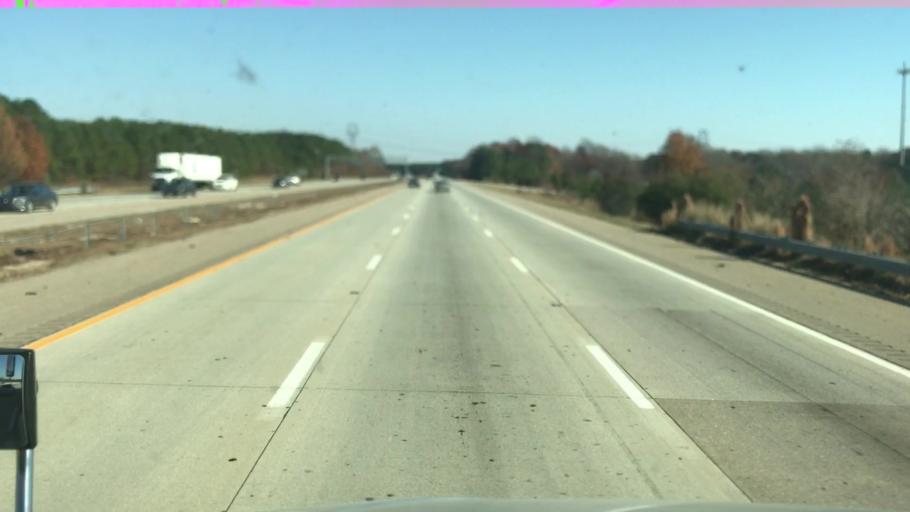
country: US
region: North Carolina
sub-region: Wake County
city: Knightdale
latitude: 35.7677
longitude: -78.4642
